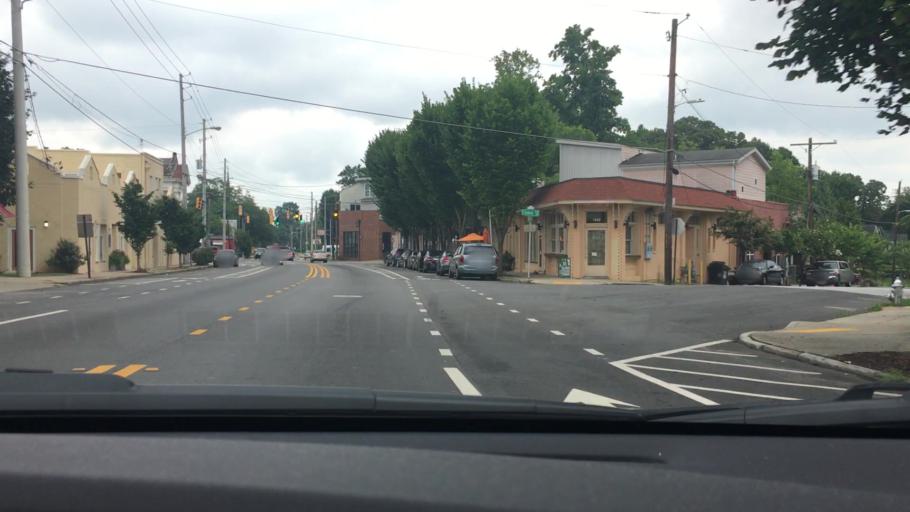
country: US
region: Georgia
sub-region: Fulton County
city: Atlanta
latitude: 33.7437
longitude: -84.4382
